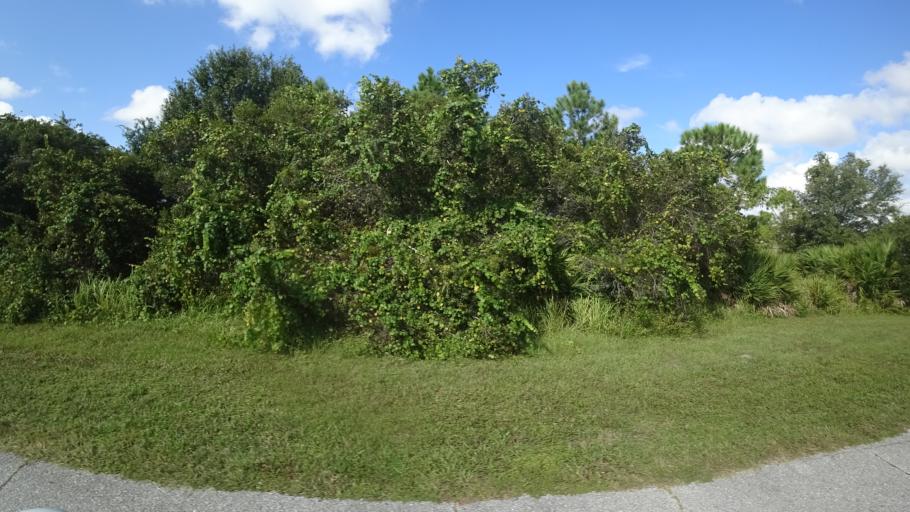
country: US
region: Florida
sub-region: Sarasota County
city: The Meadows
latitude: 27.3992
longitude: -82.3244
